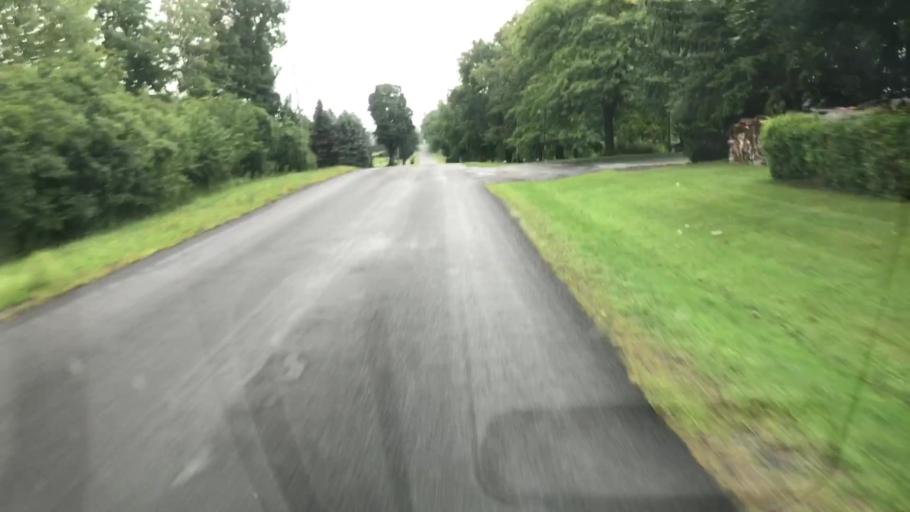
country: US
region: New York
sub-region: Cayuga County
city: Melrose Park
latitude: 42.9356
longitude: -76.5089
